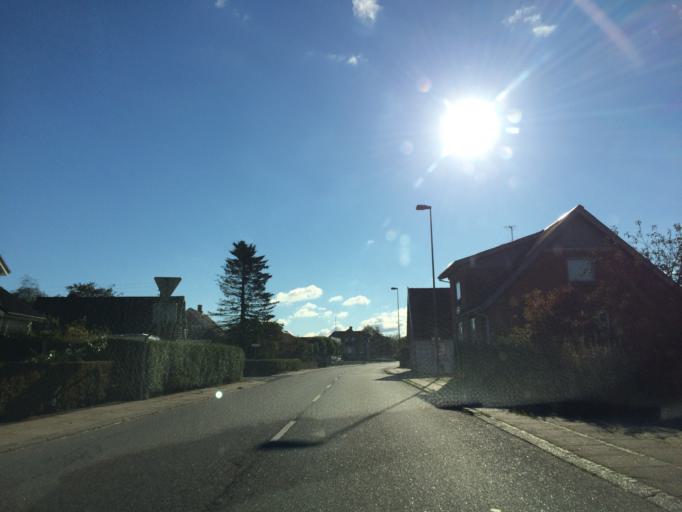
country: DK
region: Central Jutland
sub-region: Randers Kommune
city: Langa
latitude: 56.3584
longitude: 9.9137
